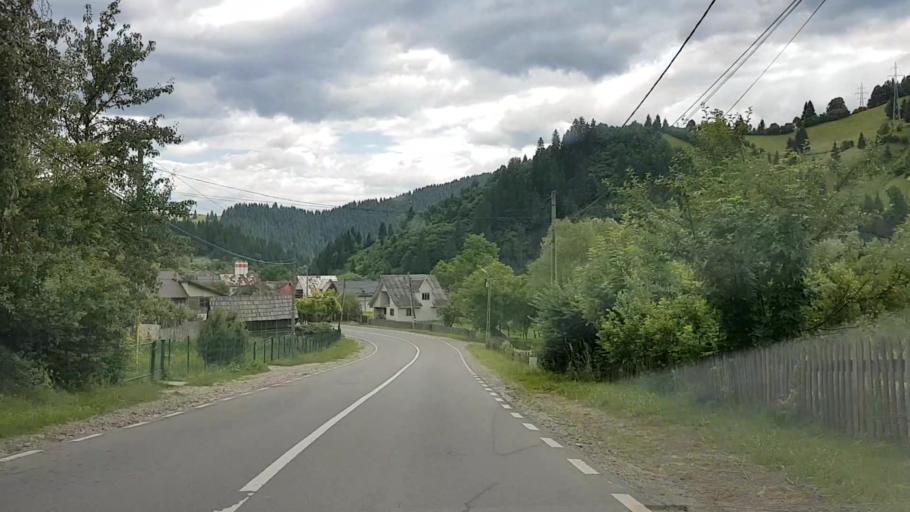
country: RO
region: Neamt
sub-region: Comuna Farcasa
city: Farcasa
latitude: 47.1585
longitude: 25.8313
